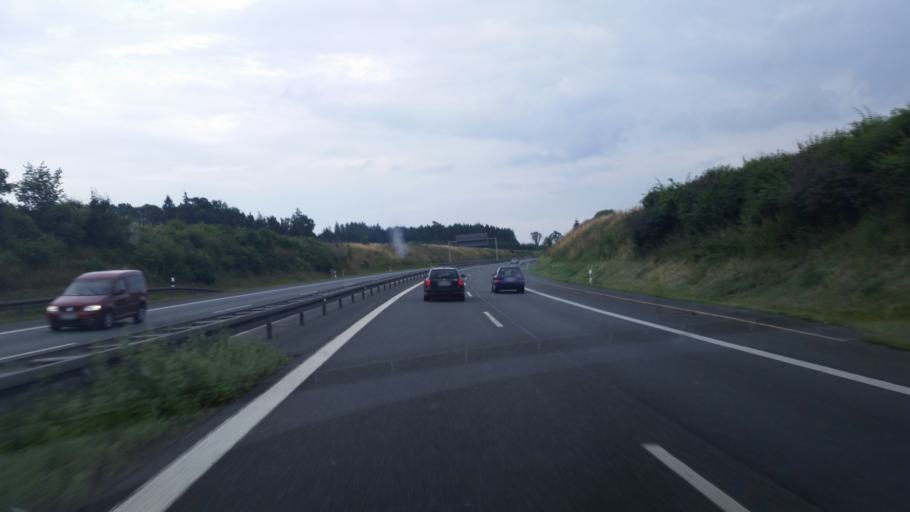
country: DE
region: Bavaria
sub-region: Upper Franconia
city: Trogen
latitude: 50.3740
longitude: 11.9723
